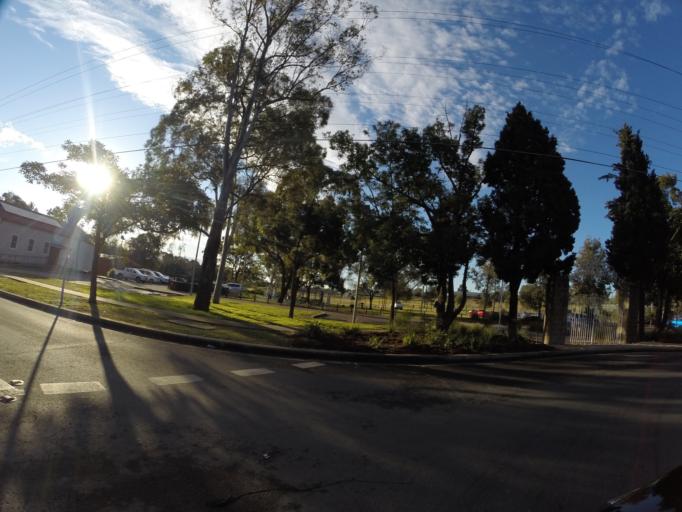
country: AU
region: New South Wales
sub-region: Fairfield
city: Horsley Park
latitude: -33.8412
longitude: 150.8463
